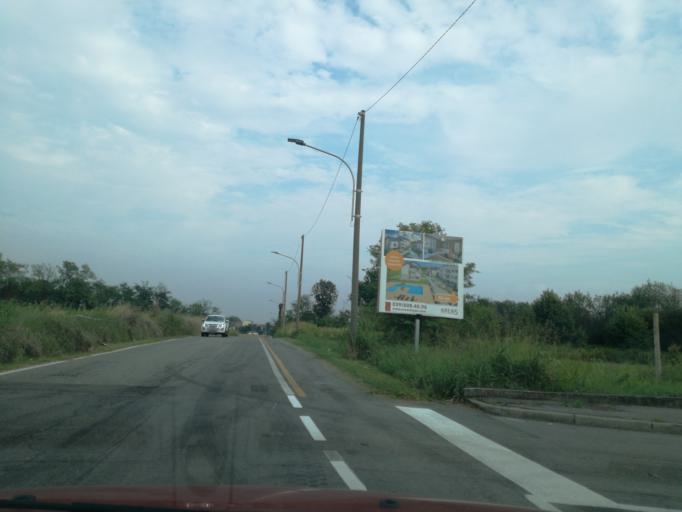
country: IT
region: Lombardy
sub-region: Provincia di Monza e Brianza
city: Carnate
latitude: 45.6423
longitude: 9.3819
